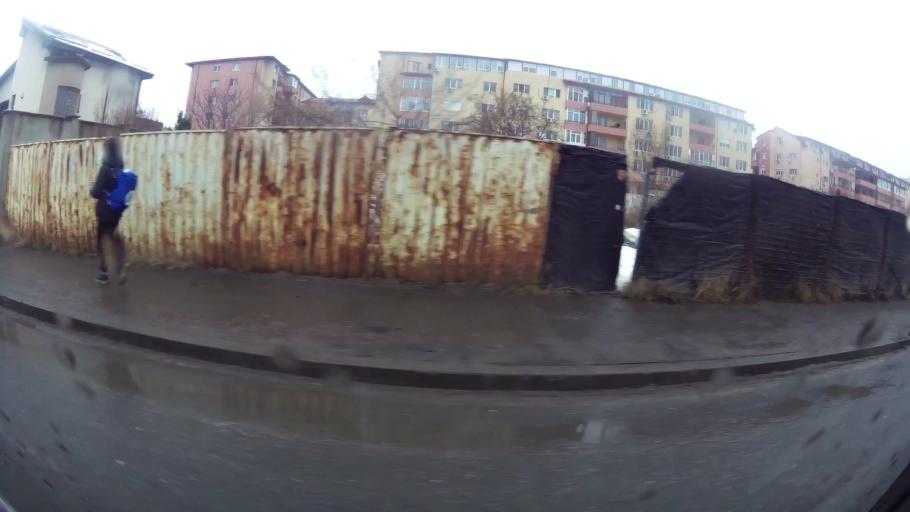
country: RO
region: Ilfov
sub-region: Comuna Chiajna
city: Rosu
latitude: 44.4105
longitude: 26.0205
